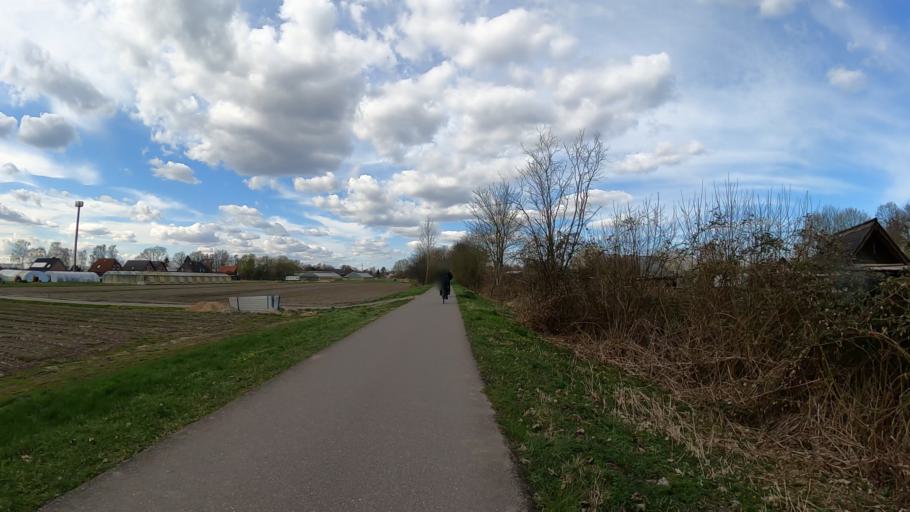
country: DE
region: Hamburg
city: Rothenburgsort
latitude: 53.4819
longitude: 10.0772
